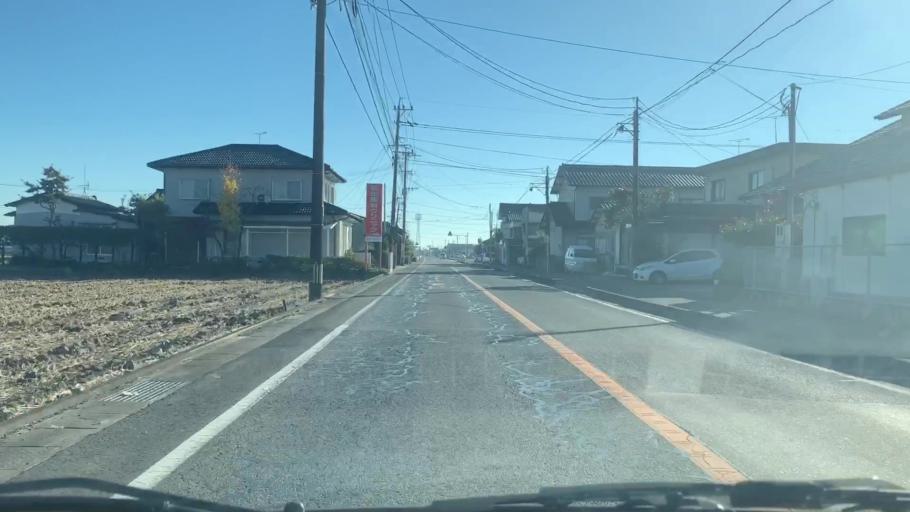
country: JP
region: Saga Prefecture
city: Kashima
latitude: 33.1833
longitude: 130.1737
